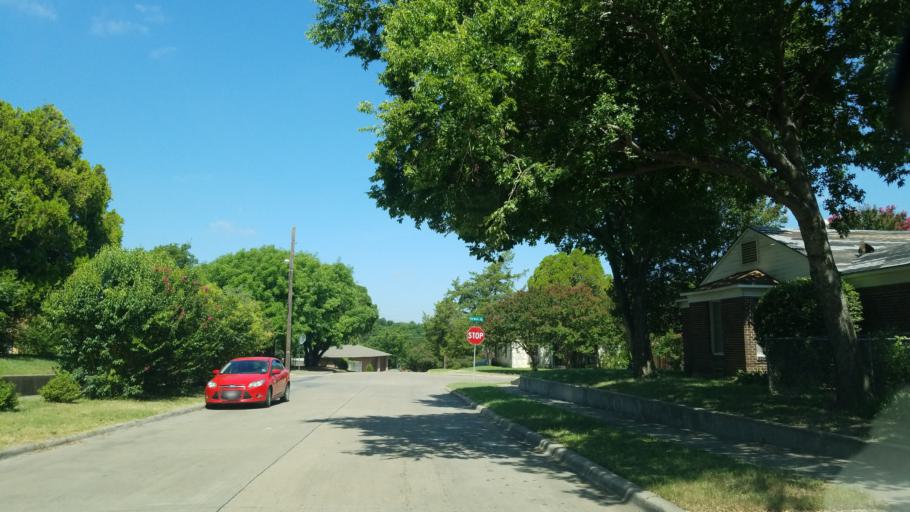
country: US
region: Texas
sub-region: Dallas County
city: Dallas
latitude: 32.7258
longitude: -96.7975
